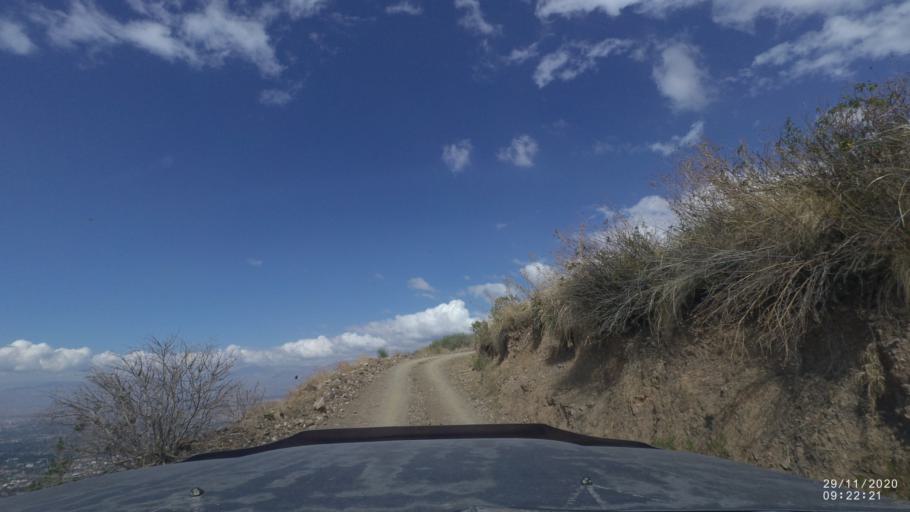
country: BO
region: Cochabamba
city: Cochabamba
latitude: -17.3227
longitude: -66.1865
